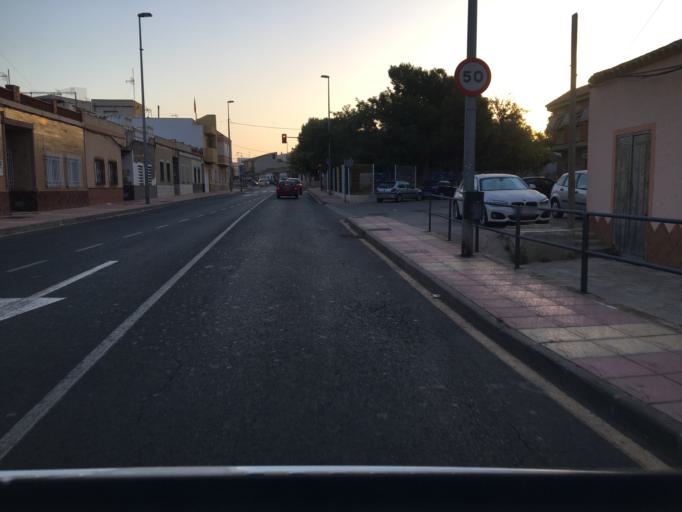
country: ES
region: Murcia
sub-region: Murcia
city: Cartagena
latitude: 37.6290
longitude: -0.9954
